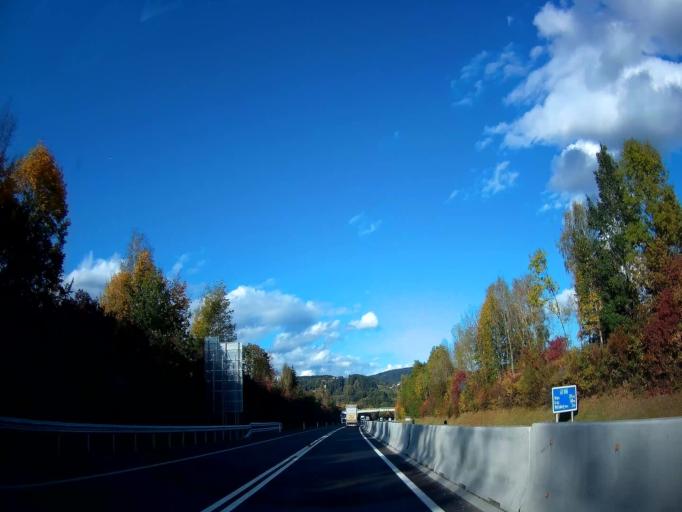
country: AT
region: Carinthia
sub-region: Politischer Bezirk Wolfsberg
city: Wolfsberg
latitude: 46.8336
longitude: 14.8190
